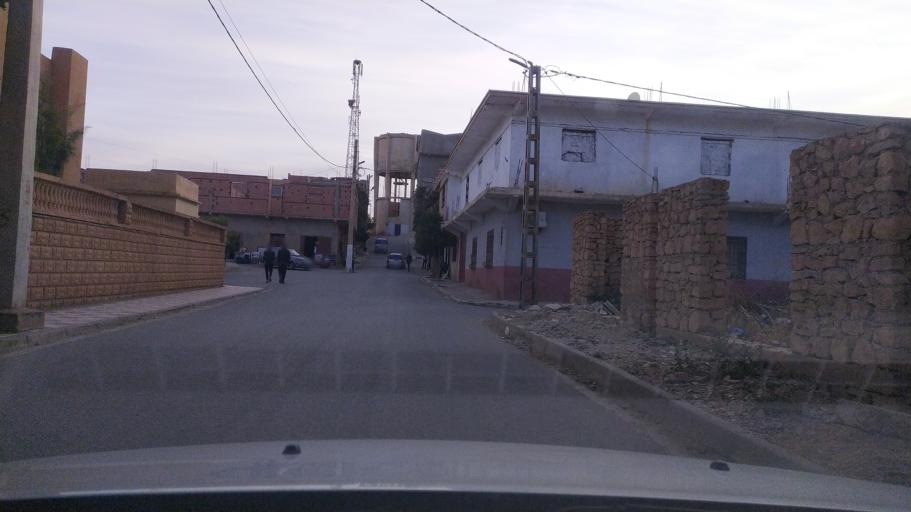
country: DZ
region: Tiaret
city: Frenda
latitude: 34.8961
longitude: 1.2398
